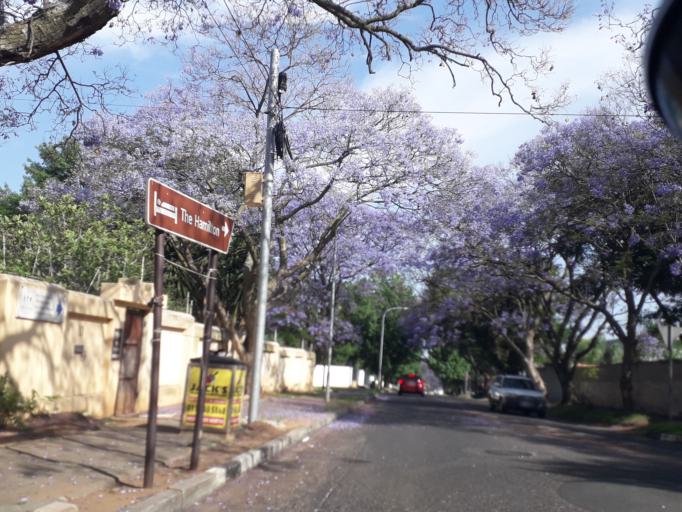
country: ZA
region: Gauteng
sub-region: City of Johannesburg Metropolitan Municipality
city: Johannesburg
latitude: -26.1257
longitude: 28.0268
